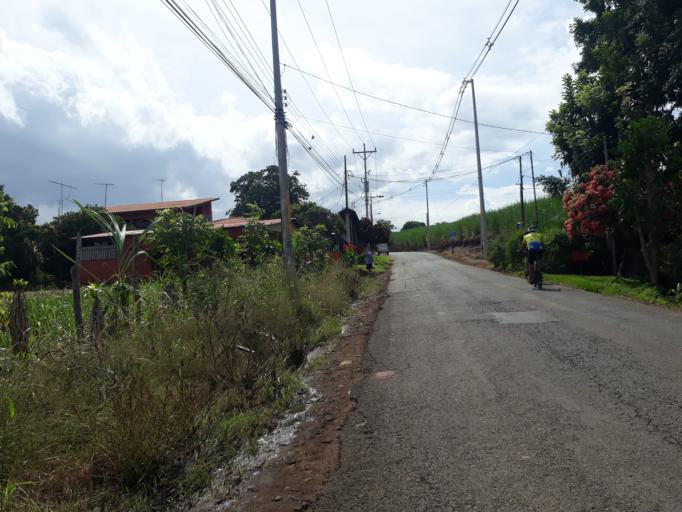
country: CR
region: Alajuela
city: Carrillos
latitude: 10.0276
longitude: -84.3347
